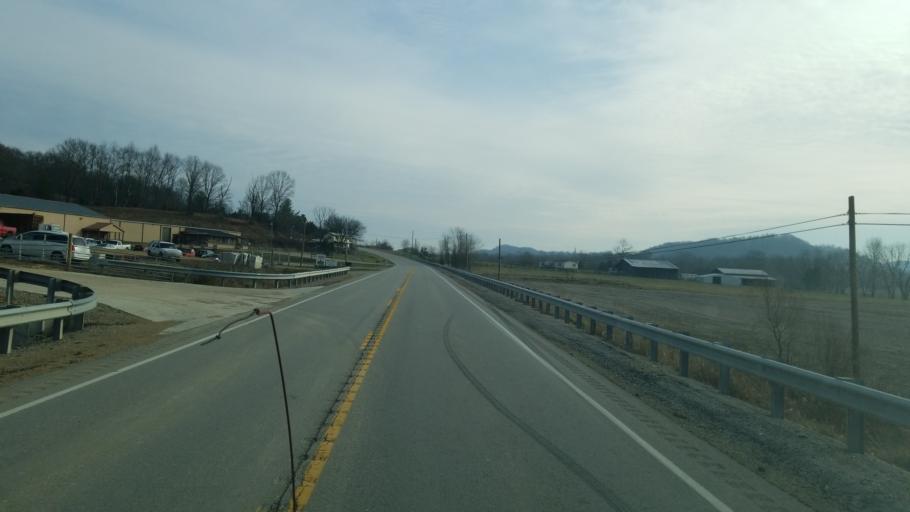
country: US
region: Kentucky
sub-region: Casey County
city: Liberty
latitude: 37.3457
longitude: -84.8863
